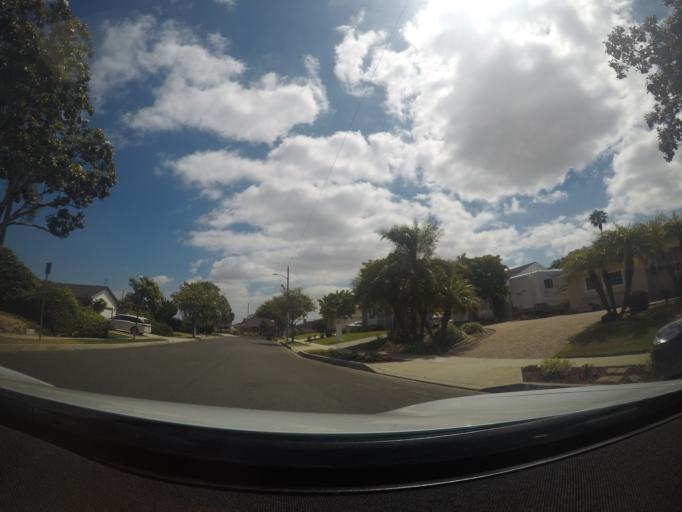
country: US
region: California
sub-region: Los Angeles County
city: Rolling Hills Estates
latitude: 33.8066
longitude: -118.3680
